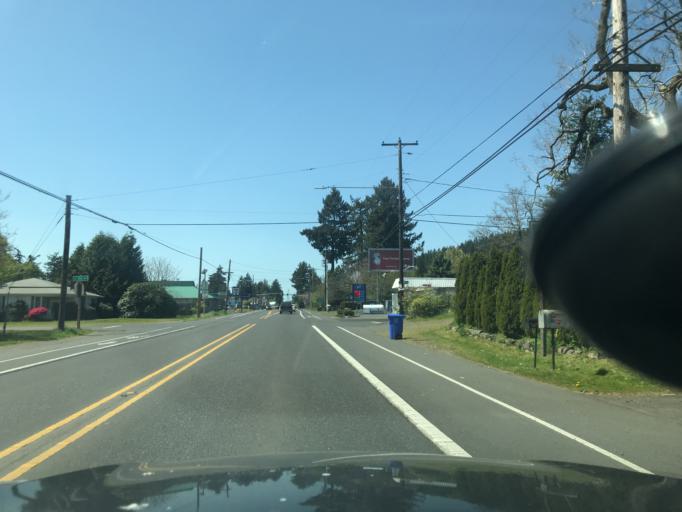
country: US
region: Oregon
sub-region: Multnomah County
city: Lents
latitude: 45.4968
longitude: -122.5449
